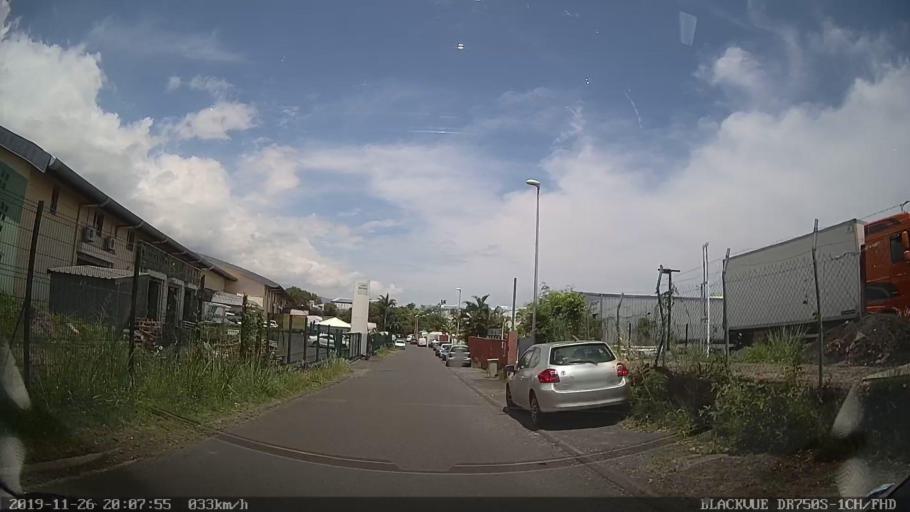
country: RE
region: Reunion
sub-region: Reunion
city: Sainte-Marie
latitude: -20.9005
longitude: 55.5322
